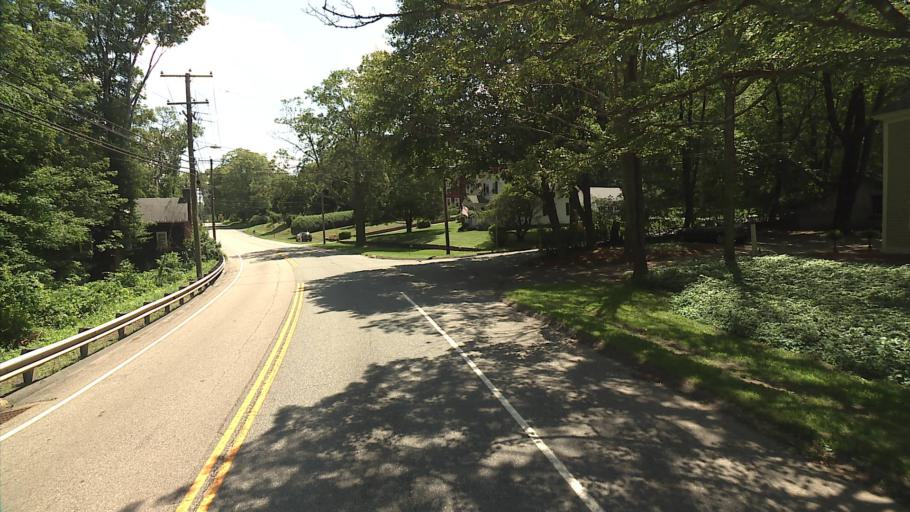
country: US
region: Connecticut
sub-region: Middlesex County
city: Chester Center
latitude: 41.3997
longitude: -72.4416
